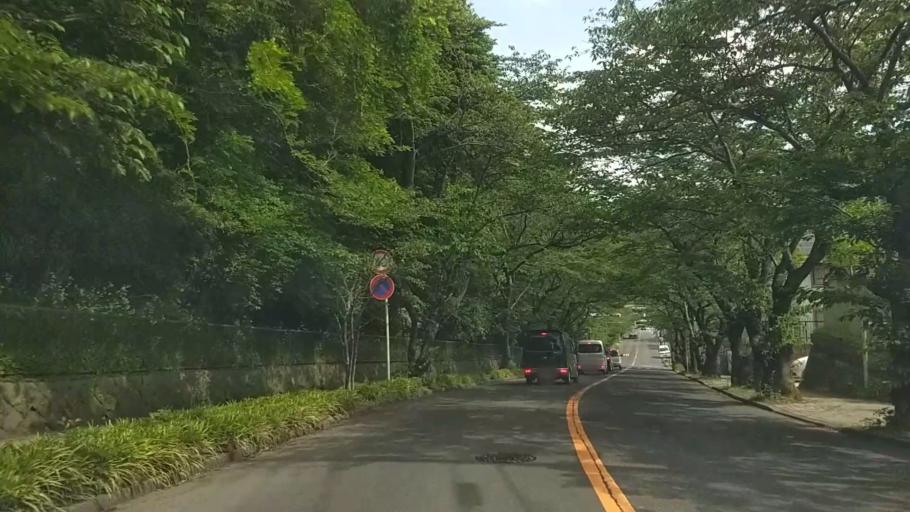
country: JP
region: Kanagawa
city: Zushi
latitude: 35.3169
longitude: 139.5767
